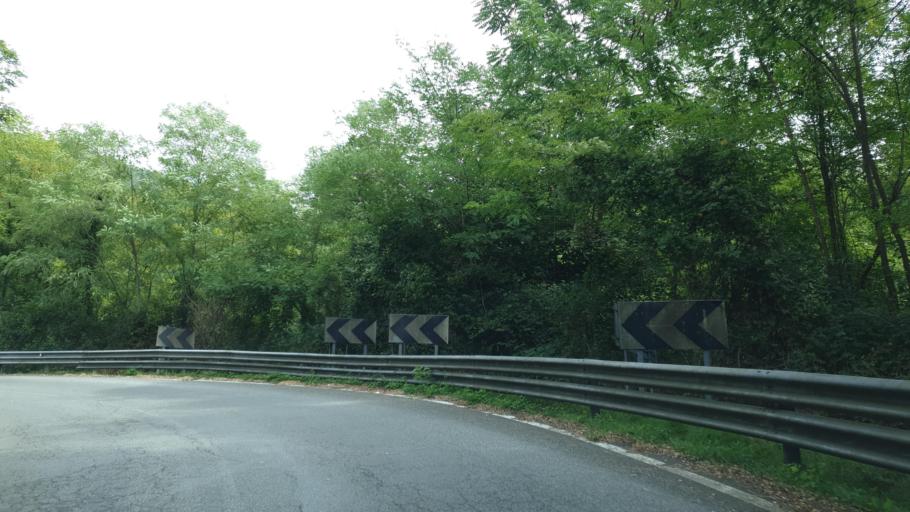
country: IT
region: Liguria
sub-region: Provincia di La Spezia
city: Carrodano
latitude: 44.2386
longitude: 9.6542
